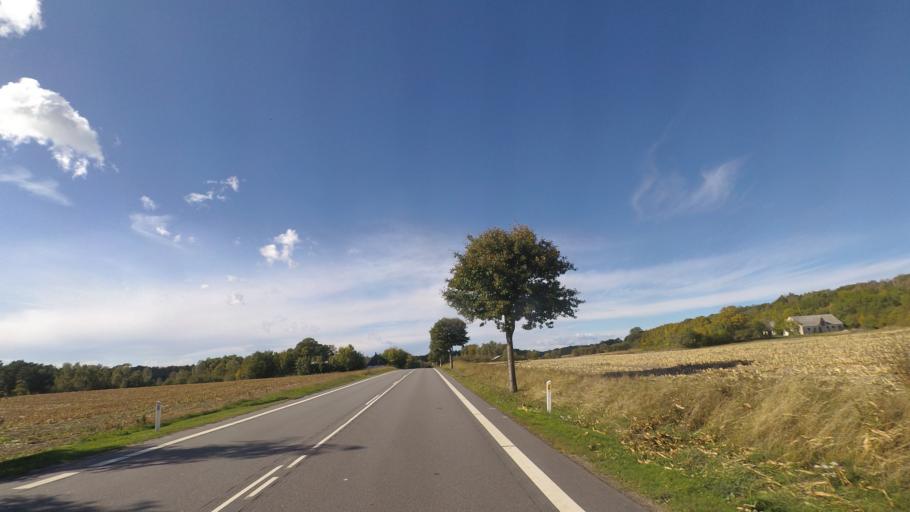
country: DK
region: Capital Region
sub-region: Bornholm Kommune
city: Ronne
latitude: 55.0783
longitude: 14.7661
